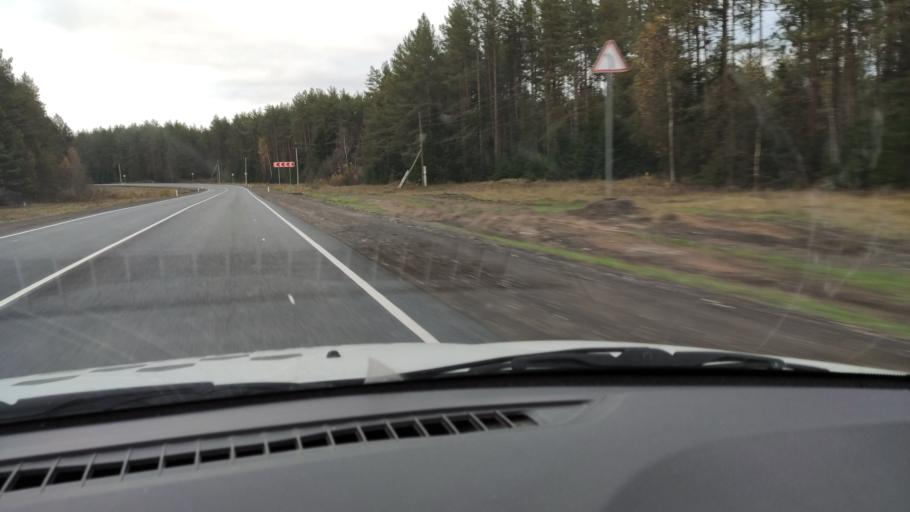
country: RU
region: Kirov
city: Belaya Kholunitsa
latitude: 58.8411
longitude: 50.7772
